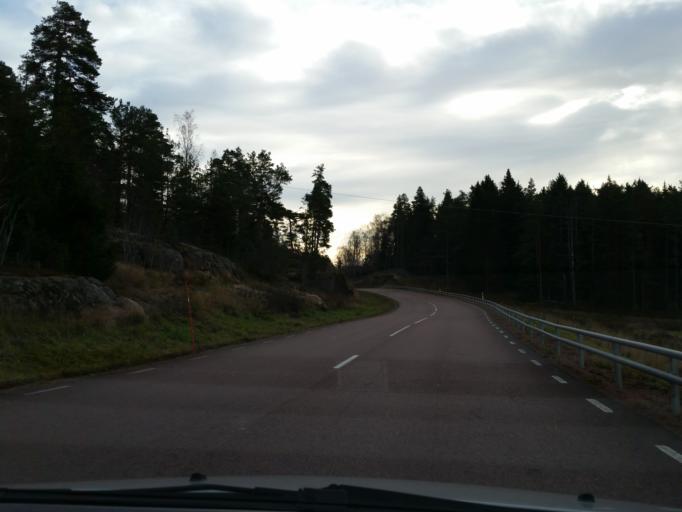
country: AX
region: Alands landsbygd
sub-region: Saltvik
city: Saltvik
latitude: 60.2497
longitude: 20.0395
